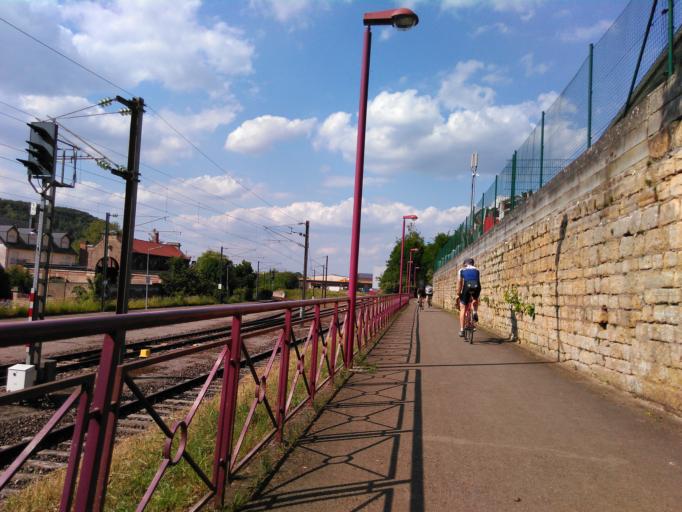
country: LU
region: Luxembourg
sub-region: Canton d'Esch-sur-Alzette
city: Rumelange
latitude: 49.4609
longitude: 6.0334
